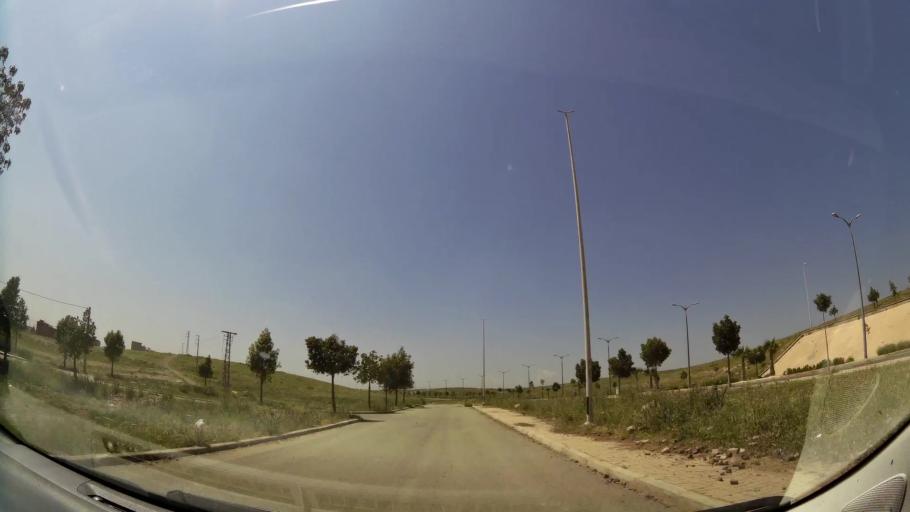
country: MA
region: Oriental
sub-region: Oujda-Angad
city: Oujda
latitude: 34.6792
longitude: -1.9471
